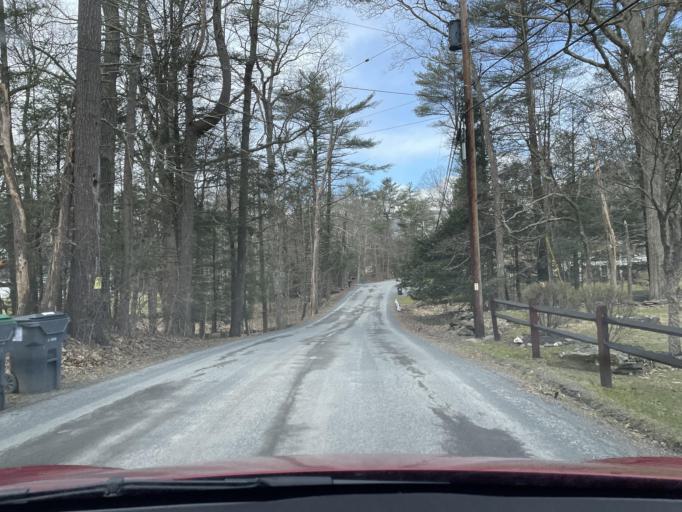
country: US
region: New York
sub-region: Ulster County
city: Manorville
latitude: 42.1087
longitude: -74.0010
